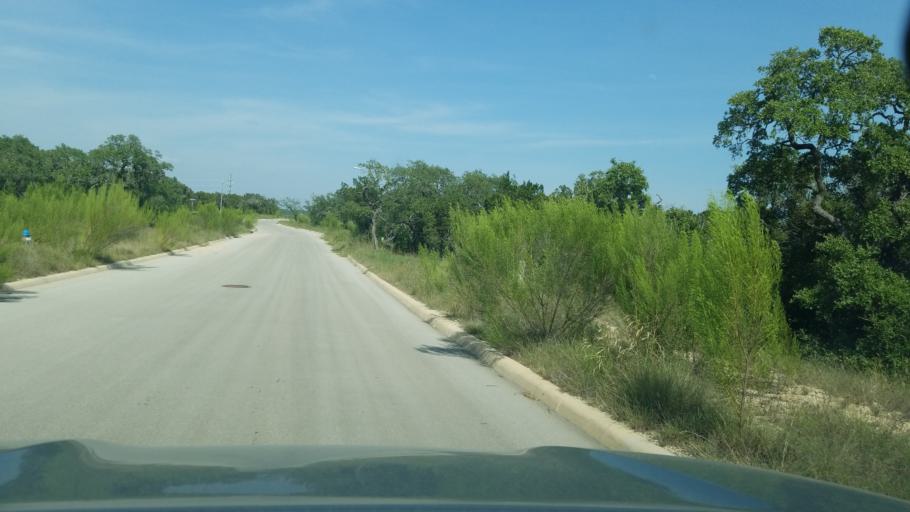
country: US
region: Texas
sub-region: Bexar County
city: Timberwood Park
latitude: 29.6949
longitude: -98.4598
